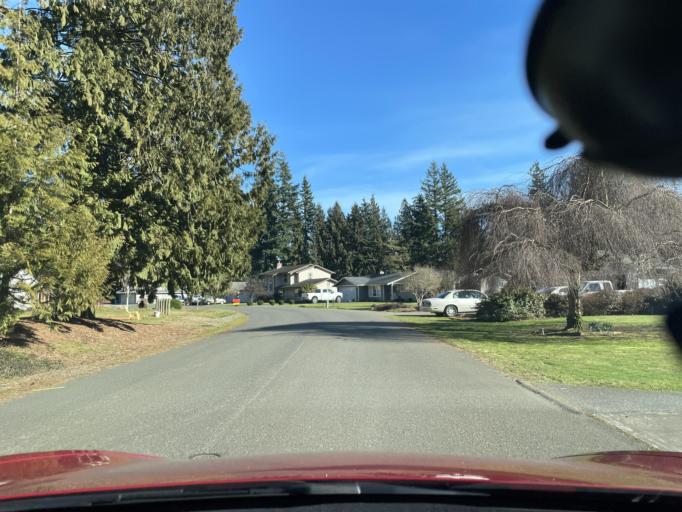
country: US
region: Washington
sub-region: Whatcom County
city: Lynden
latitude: 48.9536
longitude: -122.5105
